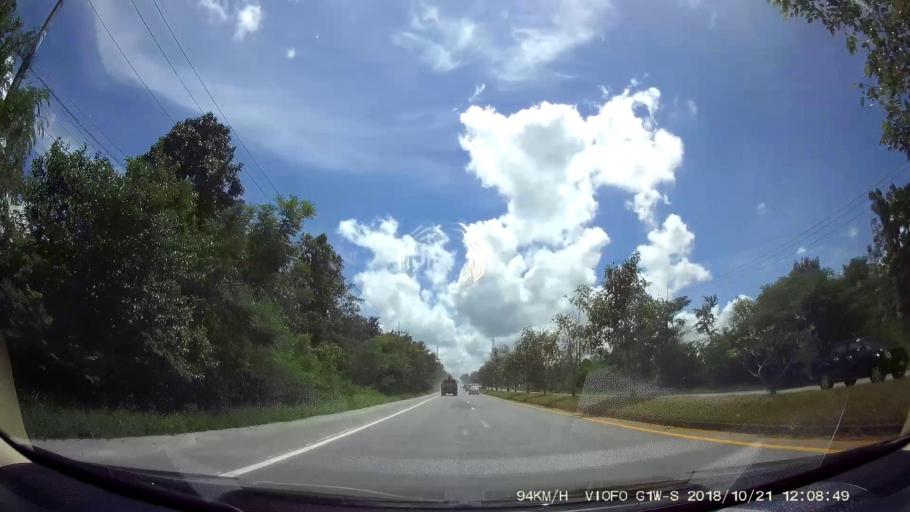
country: TH
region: Chaiyaphum
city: Chatturat
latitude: 15.4285
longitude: 101.8314
